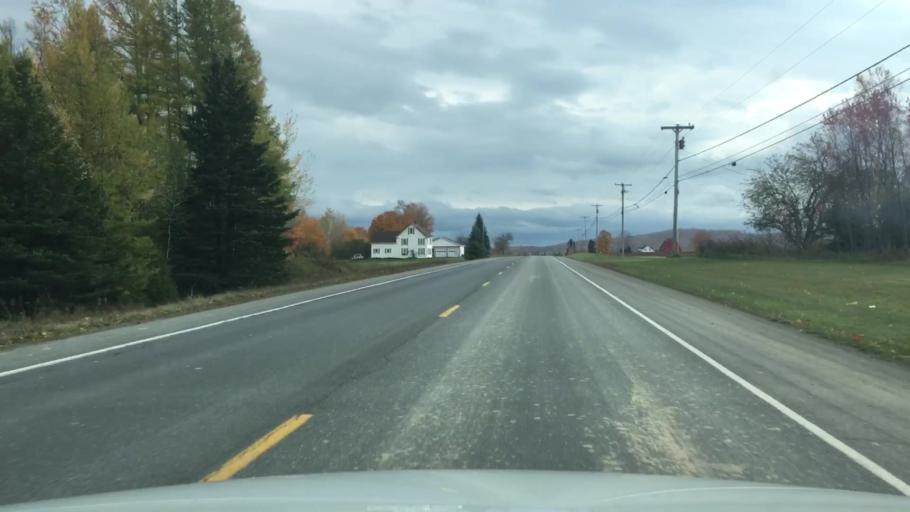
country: US
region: Maine
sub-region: Aroostook County
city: Easton
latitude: 46.5596
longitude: -67.9426
